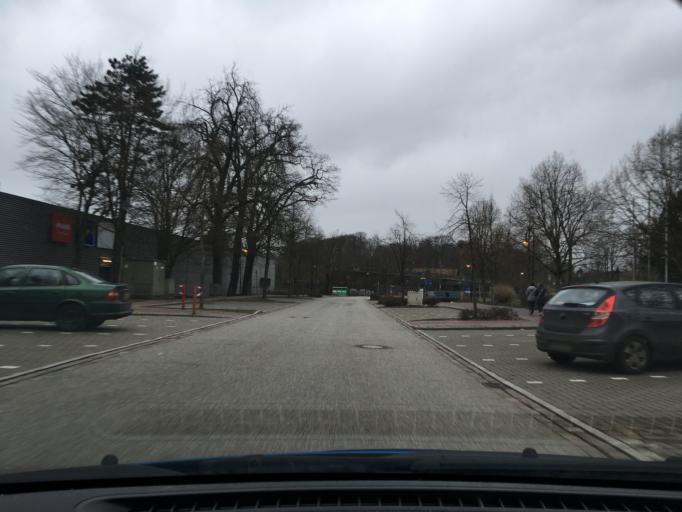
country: DE
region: Schleswig-Holstein
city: Schwarzenbek
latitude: 53.5035
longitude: 10.4789
